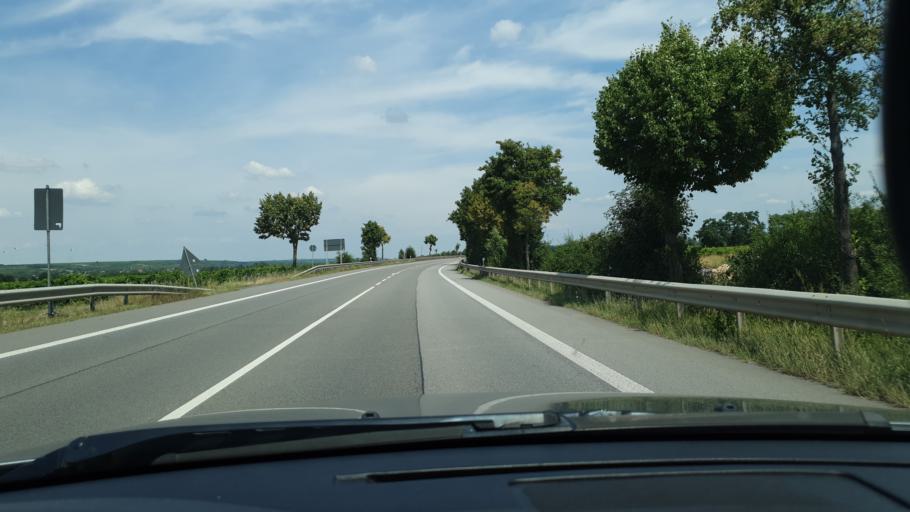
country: DE
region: Rheinland-Pfalz
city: Mettenheim
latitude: 49.7384
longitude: 8.3506
